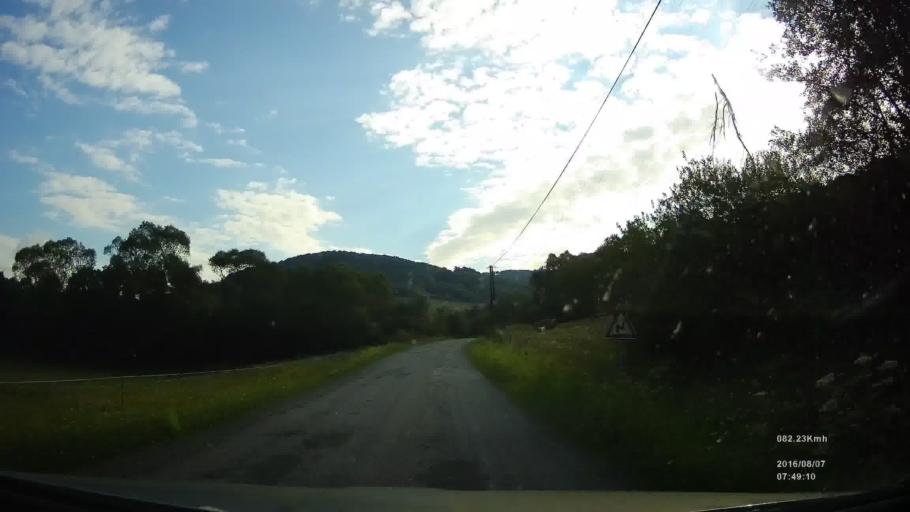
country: SK
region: Presovsky
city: Medzilaborce
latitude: 49.2894
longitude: 21.7709
